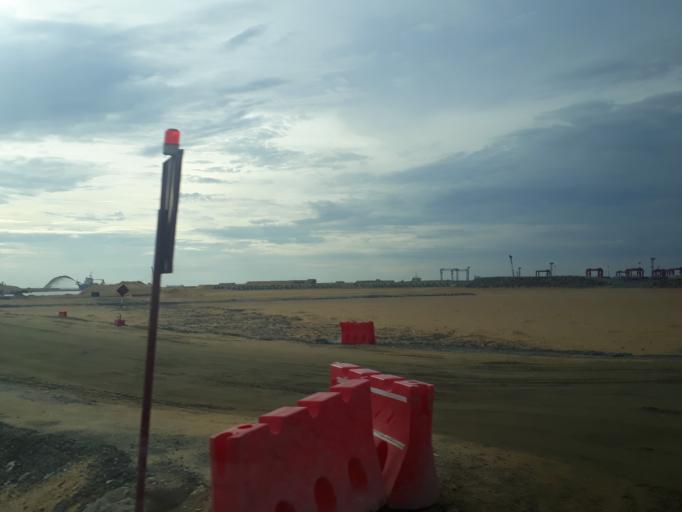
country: LK
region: Western
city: Colombo
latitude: 6.9356
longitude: 79.8377
